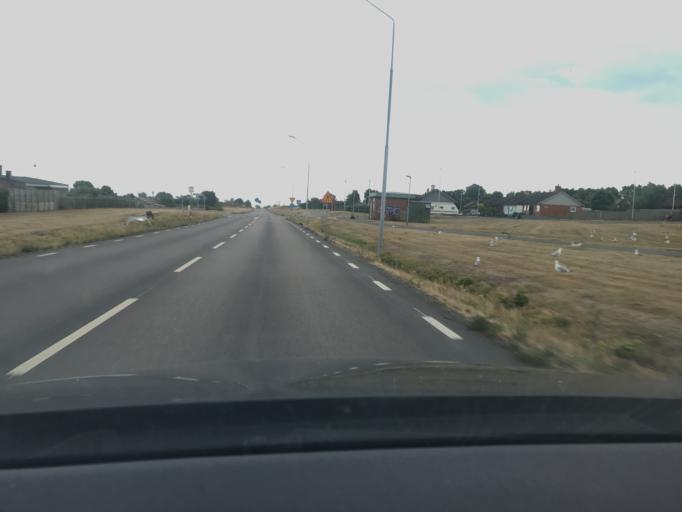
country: SE
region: Skane
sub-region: Simrishamns Kommun
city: Simrishamn
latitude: 55.5465
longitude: 14.3511
